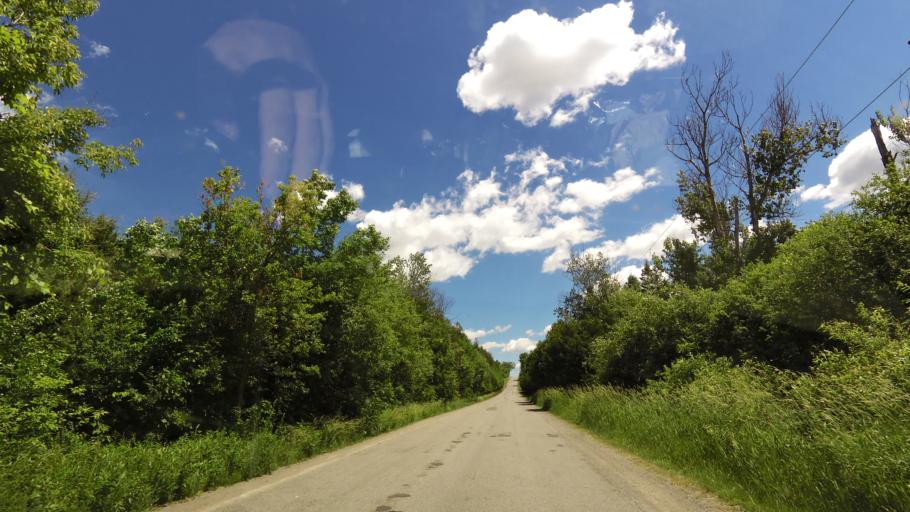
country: CA
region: Ontario
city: Omemee
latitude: 43.9748
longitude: -78.5057
